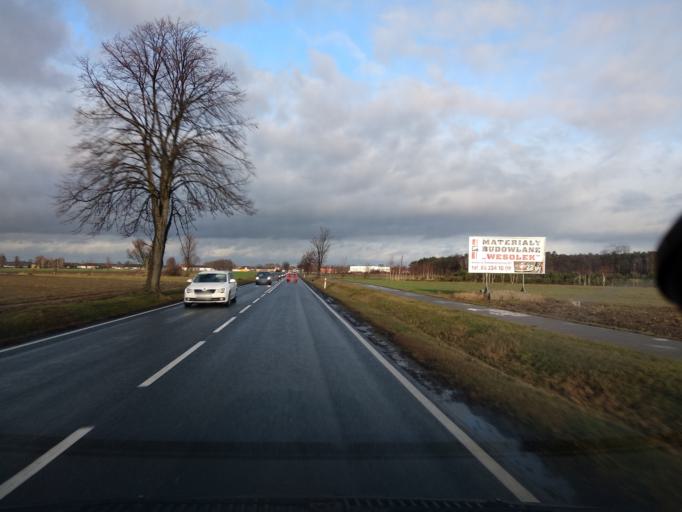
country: PL
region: Greater Poland Voivodeship
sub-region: Powiat koninski
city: Rychwal
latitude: 52.0875
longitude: 18.1635
